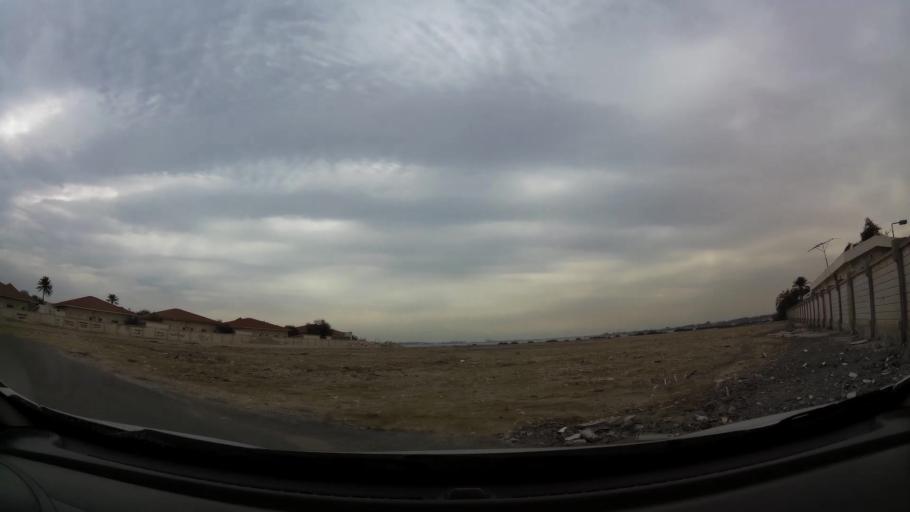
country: BH
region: Northern
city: Madinat `Isa
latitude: 26.1784
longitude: 50.5809
